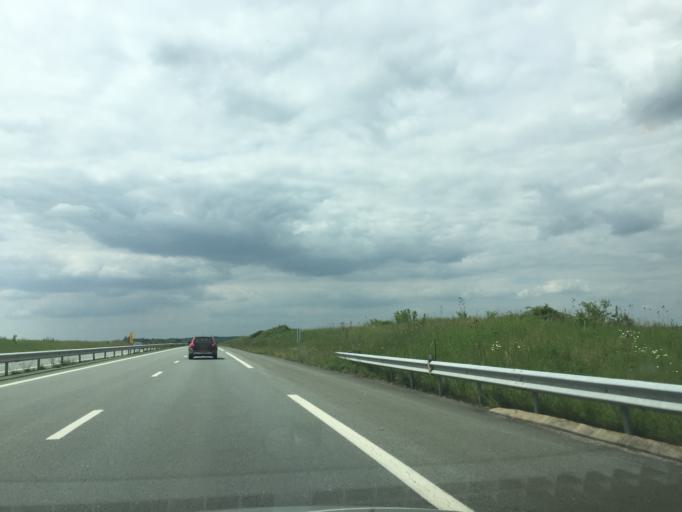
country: FR
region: Poitou-Charentes
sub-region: Departement des Deux-Sevres
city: Echire
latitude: 46.4213
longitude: -0.4291
